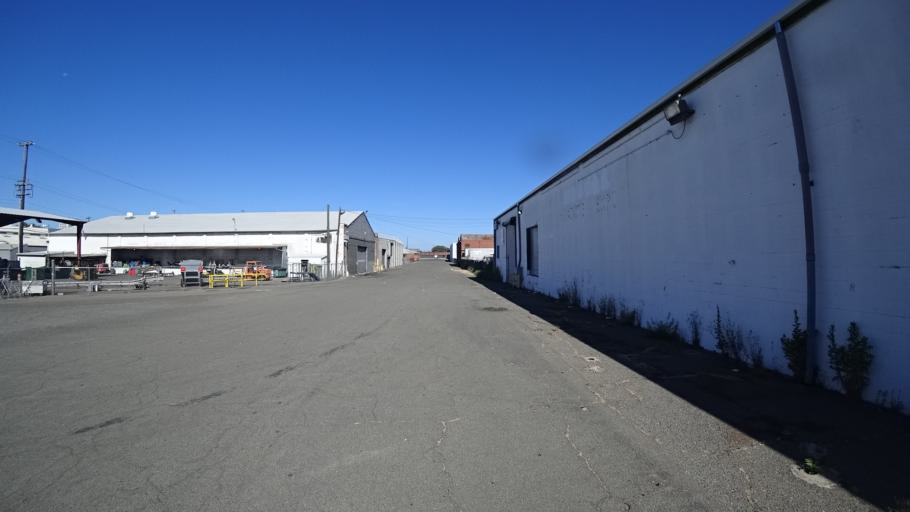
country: US
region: California
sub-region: Sacramento County
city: Sacramento
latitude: 38.5891
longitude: -121.4777
